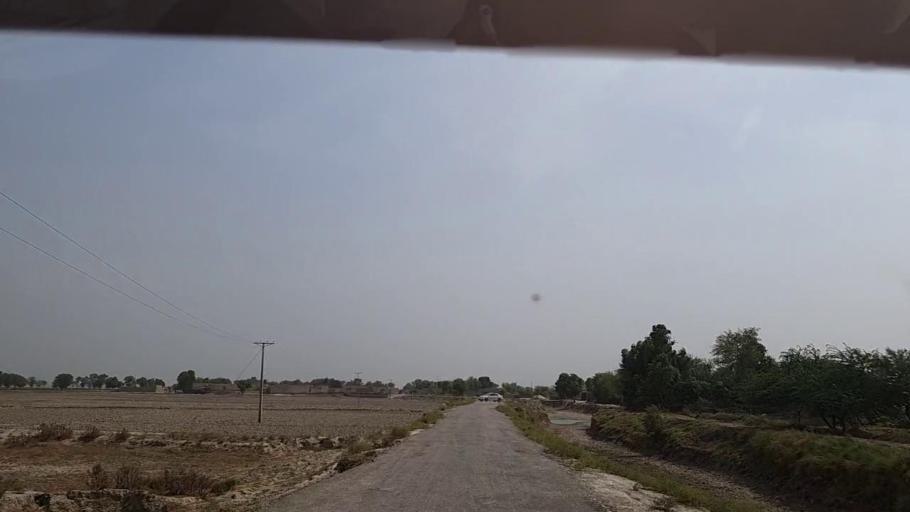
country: PK
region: Sindh
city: Khairpur Nathan Shah
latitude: 27.0690
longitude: 67.6880
